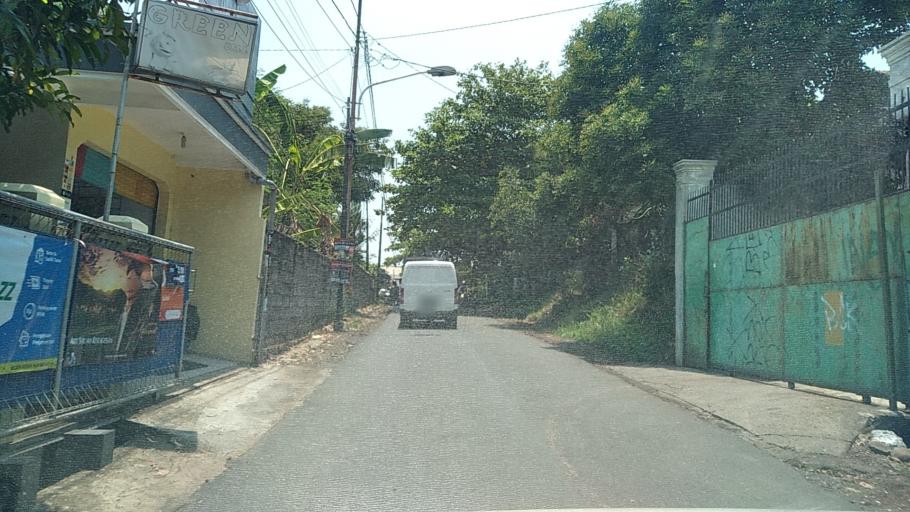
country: ID
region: Central Java
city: Semarang
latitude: -7.0009
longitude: 110.3484
